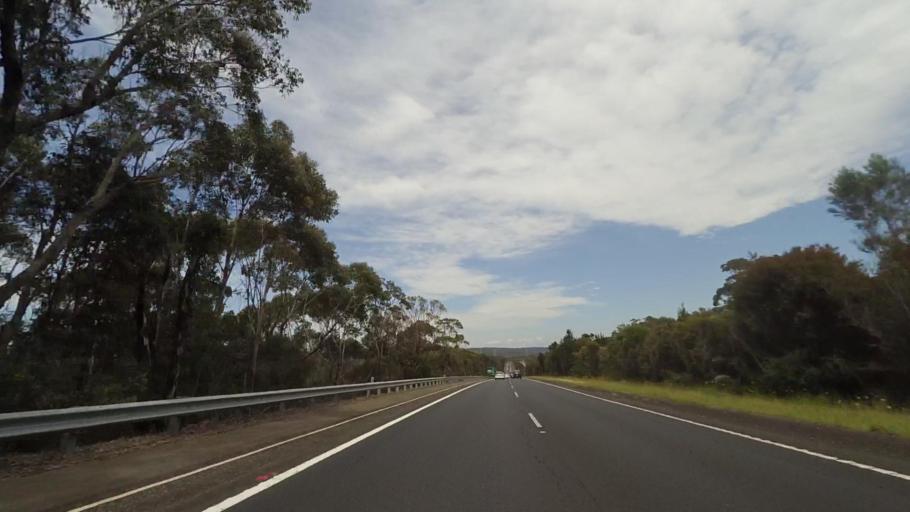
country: AU
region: New South Wales
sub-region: Wollongong
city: Helensburgh
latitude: -34.1788
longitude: 150.9755
